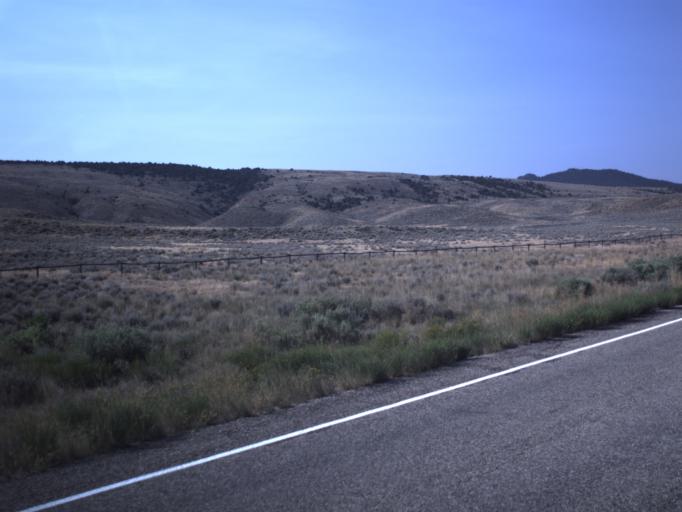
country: US
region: Utah
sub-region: Daggett County
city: Manila
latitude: 40.9802
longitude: -109.4496
